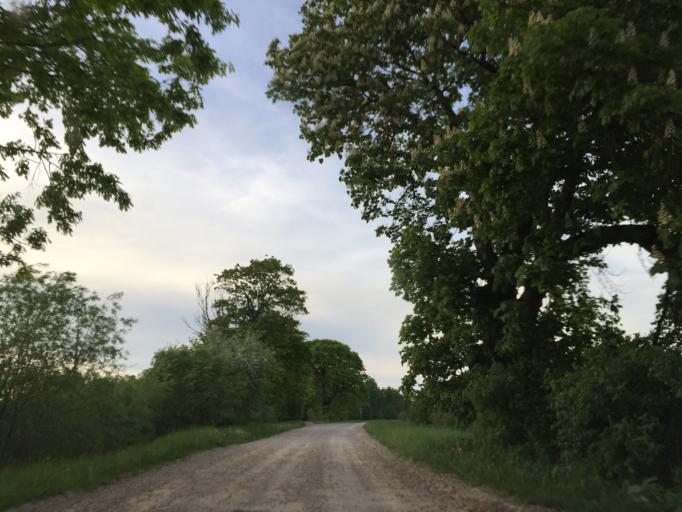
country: LV
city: Tireli
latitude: 56.7129
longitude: 23.4965
